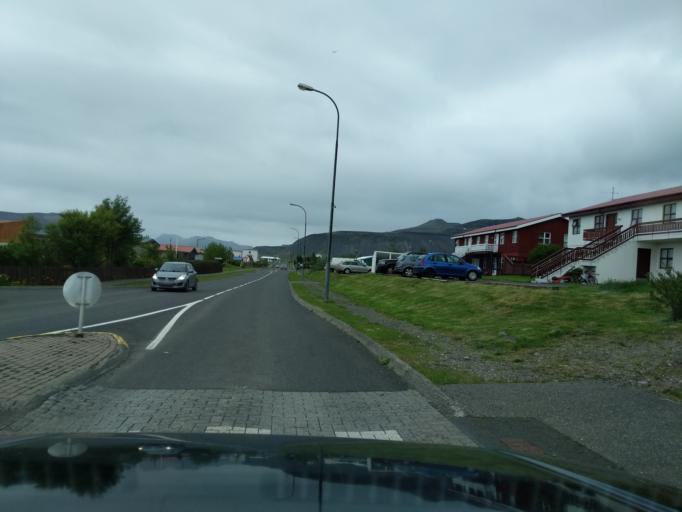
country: IS
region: West
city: Olafsvik
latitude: 64.9238
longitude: -23.2712
